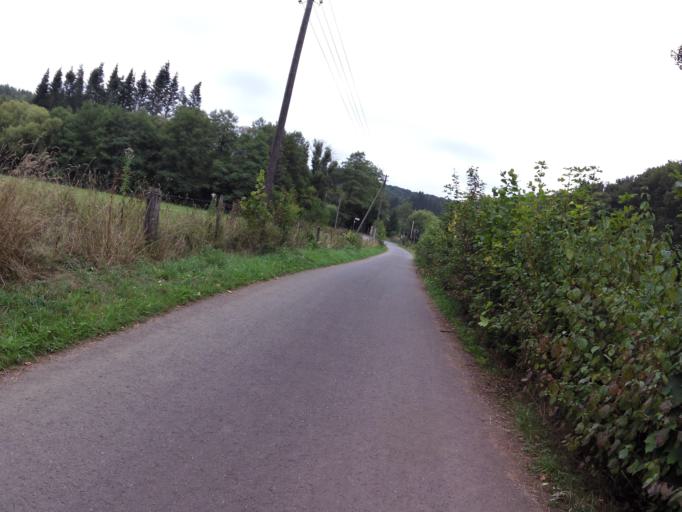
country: DE
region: North Rhine-Westphalia
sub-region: Regierungsbezirk Koln
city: Nettersheim
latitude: 50.5114
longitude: 6.5947
